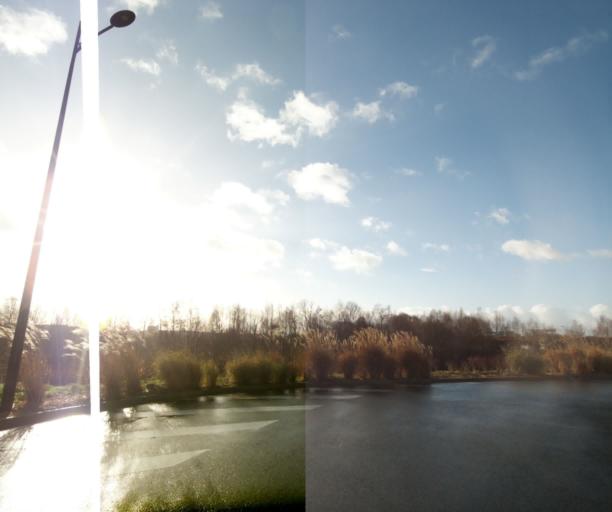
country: FR
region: Pays de la Loire
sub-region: Departement de la Sarthe
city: Coulaines
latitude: 48.0305
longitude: 0.1845
